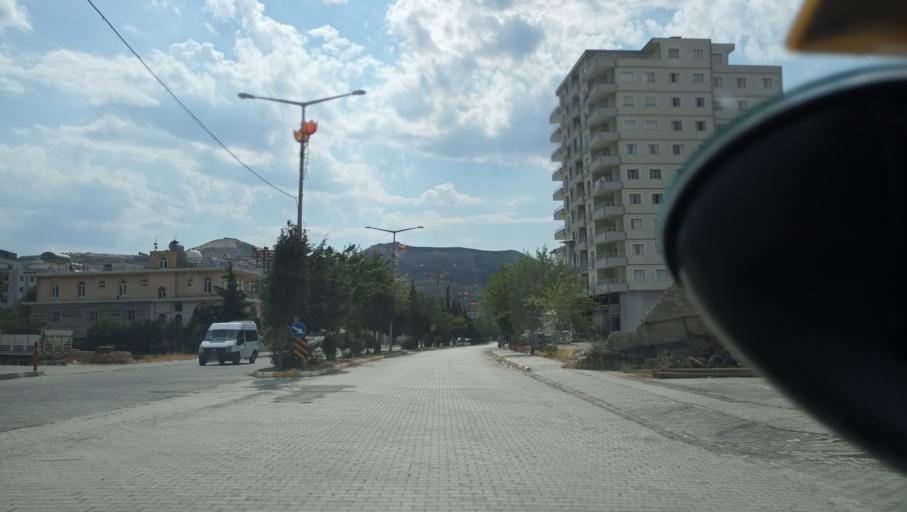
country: TR
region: Mardin
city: Kabala
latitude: 37.3402
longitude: 40.8133
